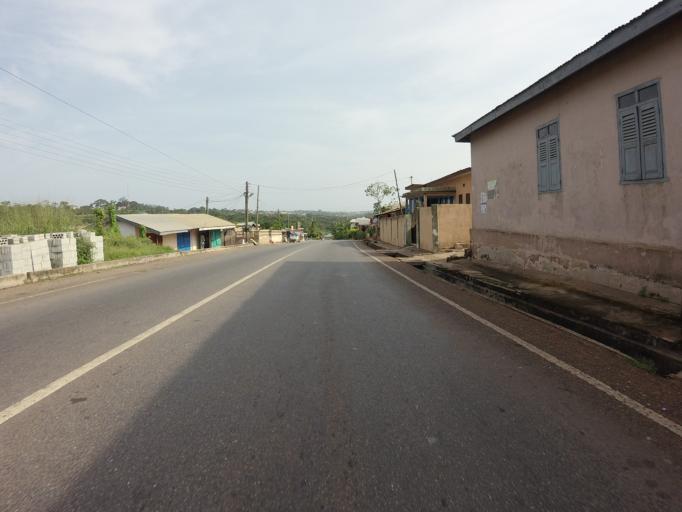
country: GH
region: Eastern
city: Aburi
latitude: 5.8750
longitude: -0.1572
